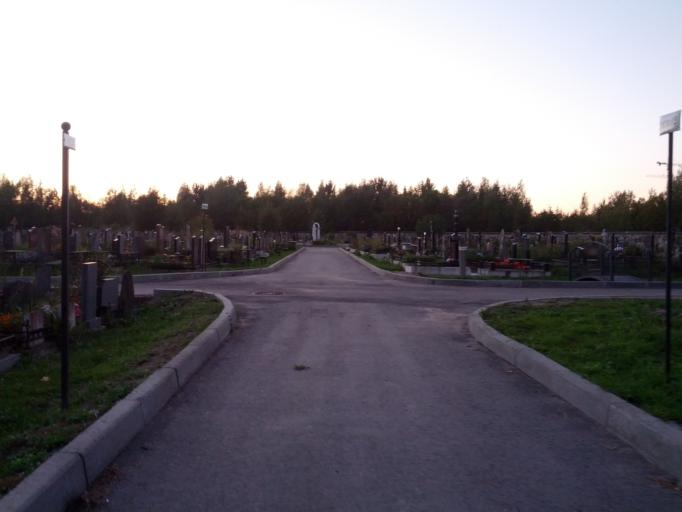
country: RU
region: St.-Petersburg
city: Obukhovo
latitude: 59.9130
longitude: 30.4320
